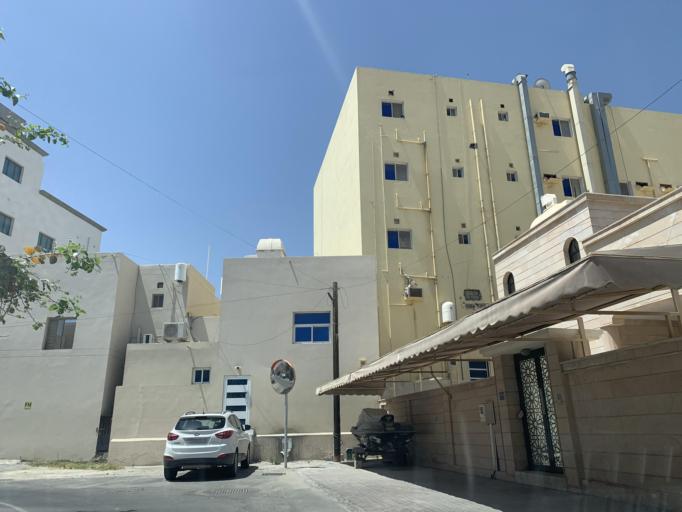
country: BH
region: Northern
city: Ar Rifa'
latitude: 26.1322
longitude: 50.5789
